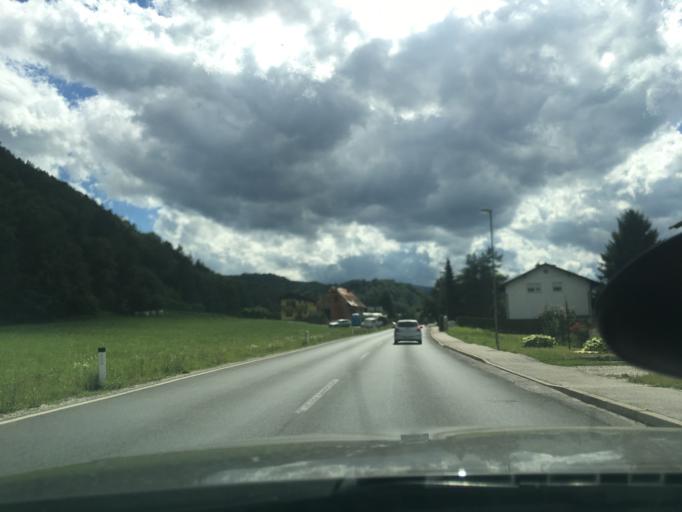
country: SI
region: Ruse
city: Bistrica ob Dravi
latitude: 46.5571
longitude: 15.5592
